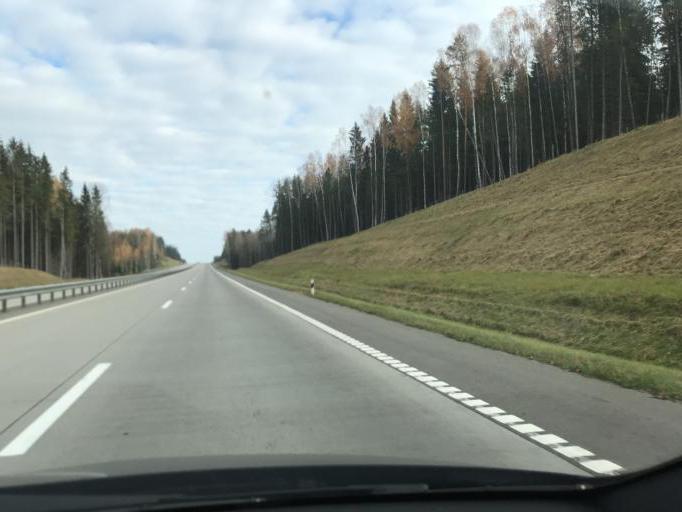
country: BY
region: Minsk
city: Rakaw
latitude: 53.9901
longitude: 27.1101
